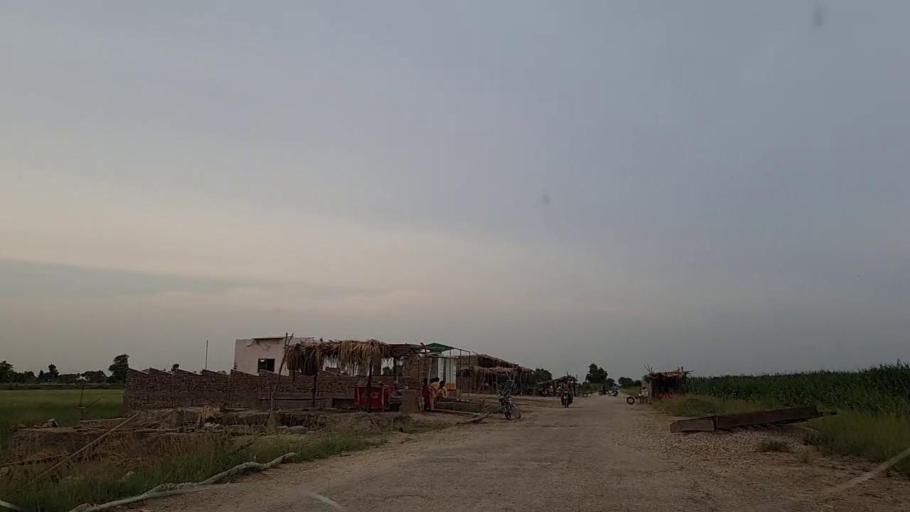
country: PK
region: Sindh
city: Mirpur Mathelo
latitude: 27.8799
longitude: 69.6374
